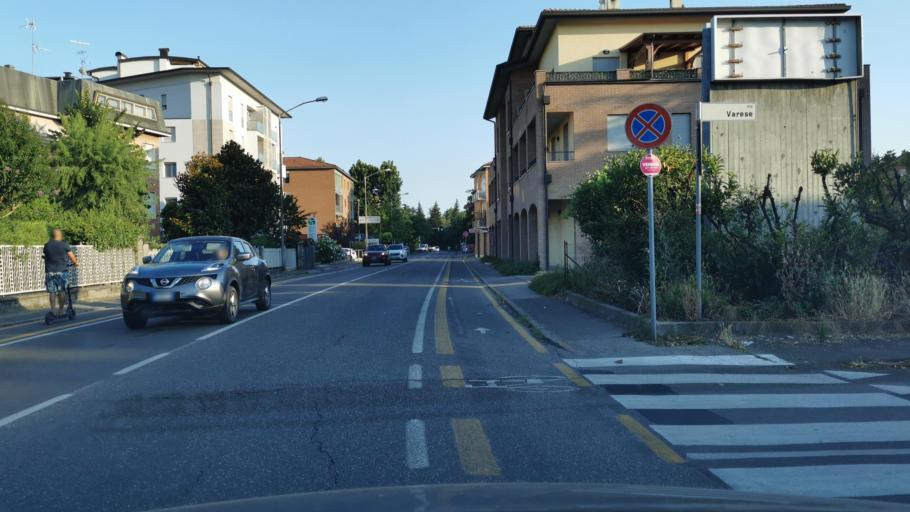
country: IT
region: Emilia-Romagna
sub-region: Provincia di Modena
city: Modena
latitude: 44.6259
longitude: 10.9272
